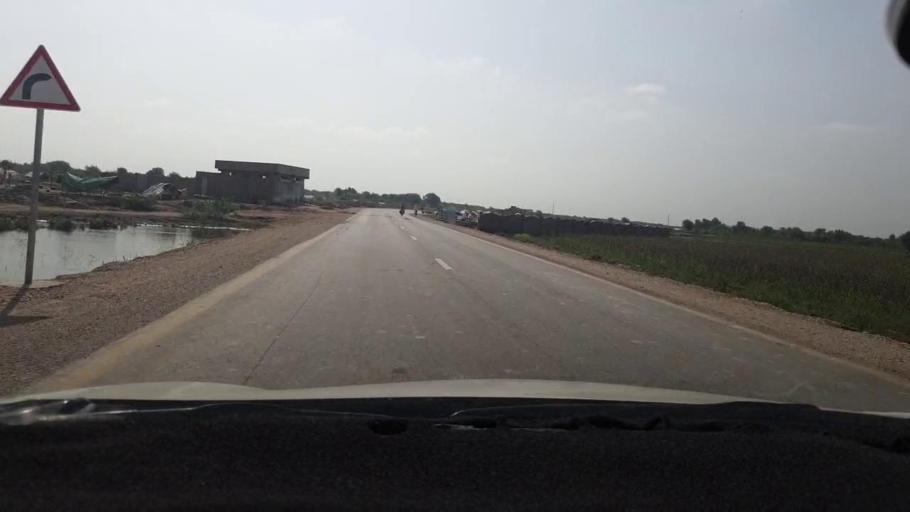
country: PK
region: Sindh
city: Tando Mittha Khan
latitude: 25.8106
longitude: 69.0710
